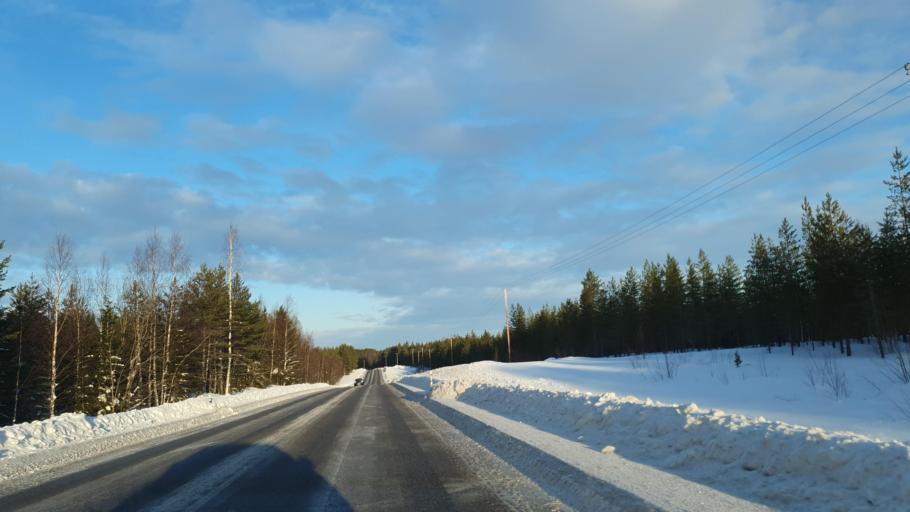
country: FI
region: Kainuu
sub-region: Kajaani
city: Vaala
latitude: 64.5414
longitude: 27.1867
